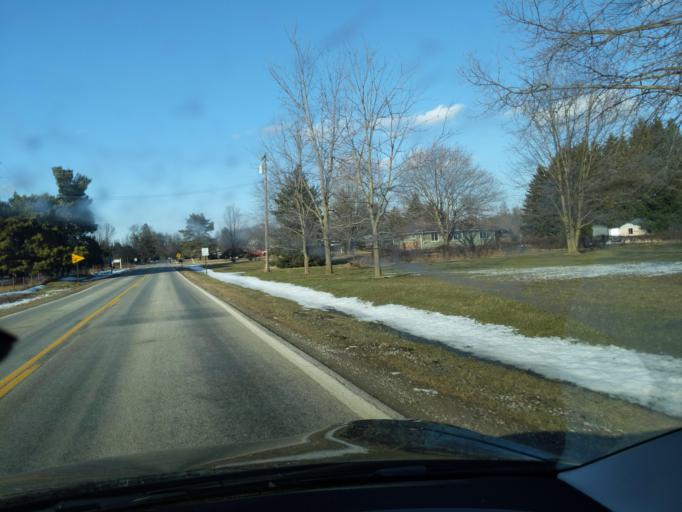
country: US
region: Michigan
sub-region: Ingham County
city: Stockbridge
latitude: 42.5205
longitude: -84.0706
